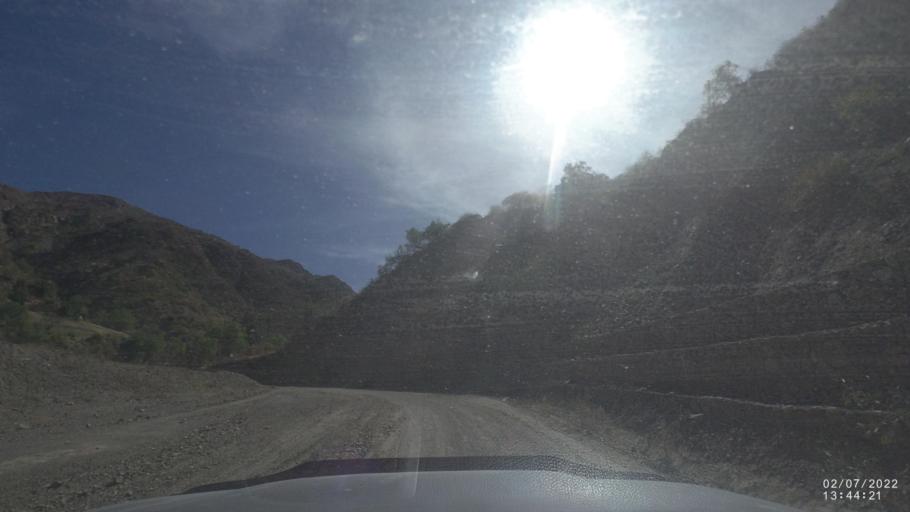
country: BO
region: Cochabamba
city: Irpa Irpa
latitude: -17.8049
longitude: -66.3644
